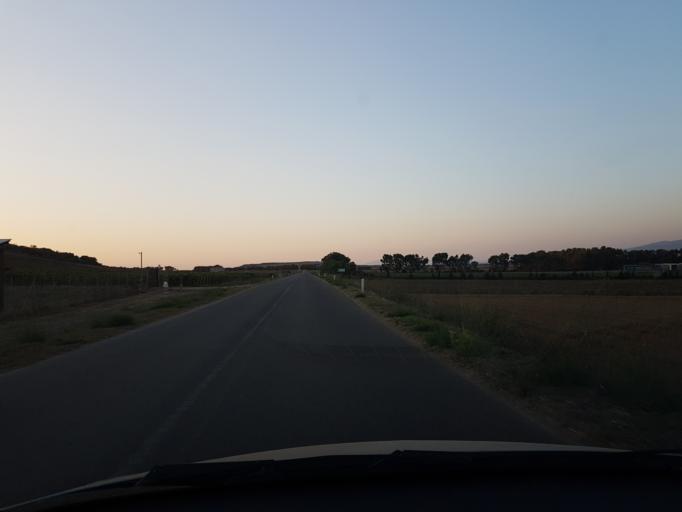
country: IT
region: Sardinia
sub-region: Provincia di Oristano
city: Cabras
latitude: 39.9632
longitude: 8.4538
